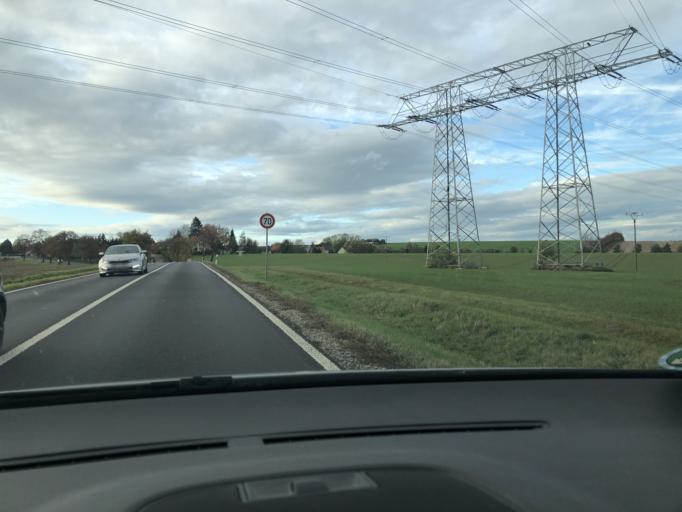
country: DE
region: Thuringia
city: Frankendorf
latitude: 50.9659
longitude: 11.4568
